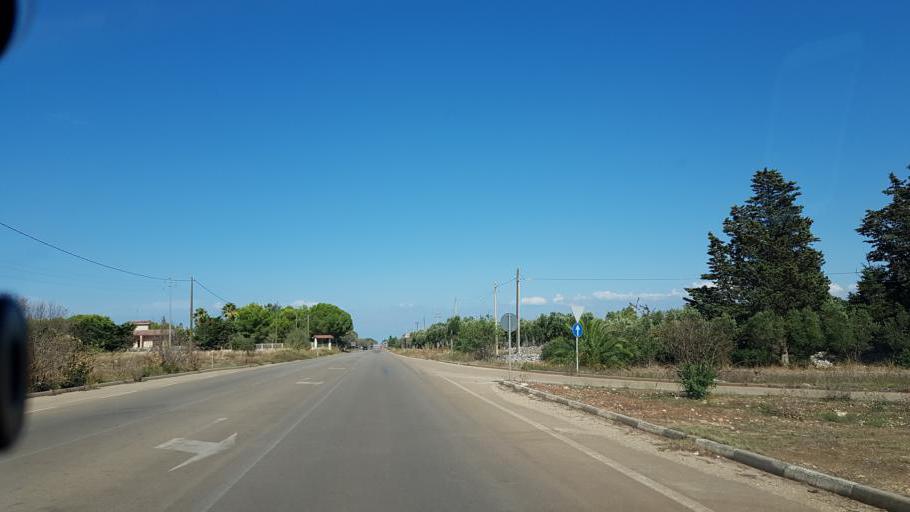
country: IT
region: Apulia
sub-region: Provincia di Lecce
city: Leverano
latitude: 40.2413
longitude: 17.9693
